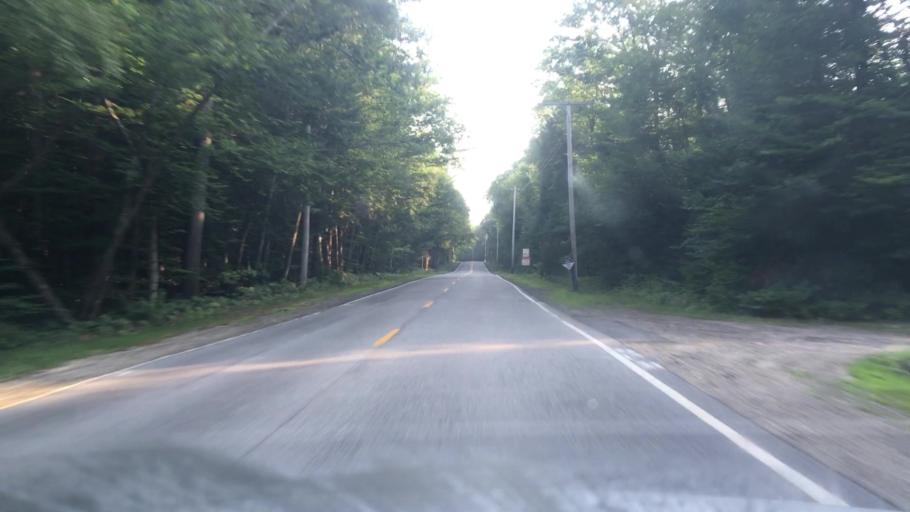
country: US
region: Maine
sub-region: Androscoggin County
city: Lisbon Falls
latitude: 43.9292
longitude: -70.0864
